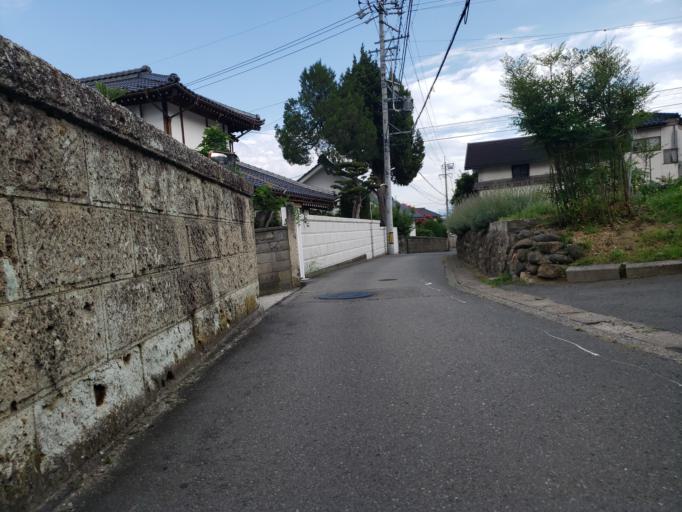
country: JP
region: Nagano
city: Nagano-shi
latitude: 36.6410
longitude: 138.1748
